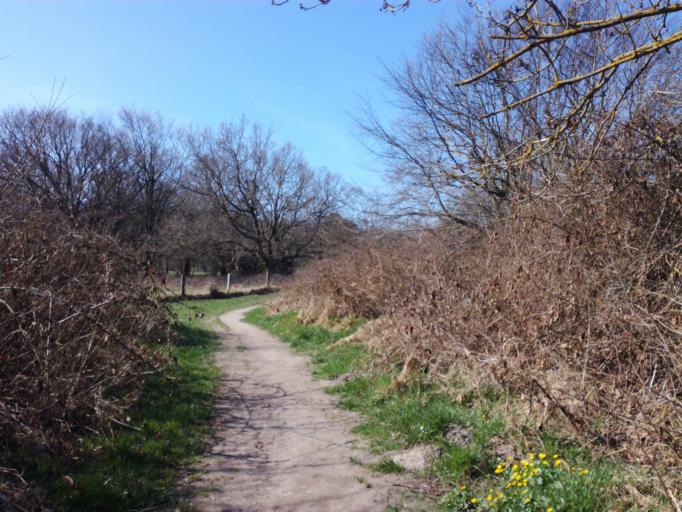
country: DK
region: South Denmark
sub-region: Fredericia Kommune
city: Fredericia
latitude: 55.6254
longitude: 9.8567
